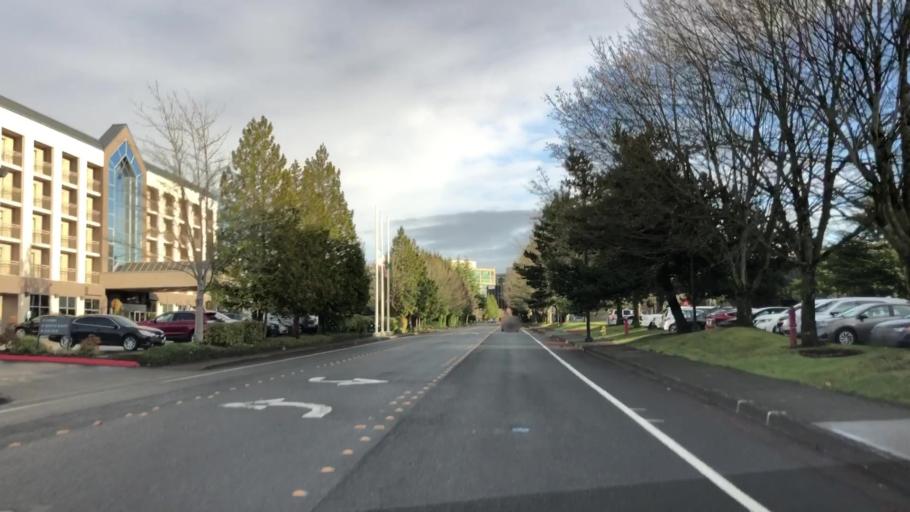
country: US
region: Washington
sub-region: King County
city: Eastgate
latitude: 47.5802
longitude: -122.1342
